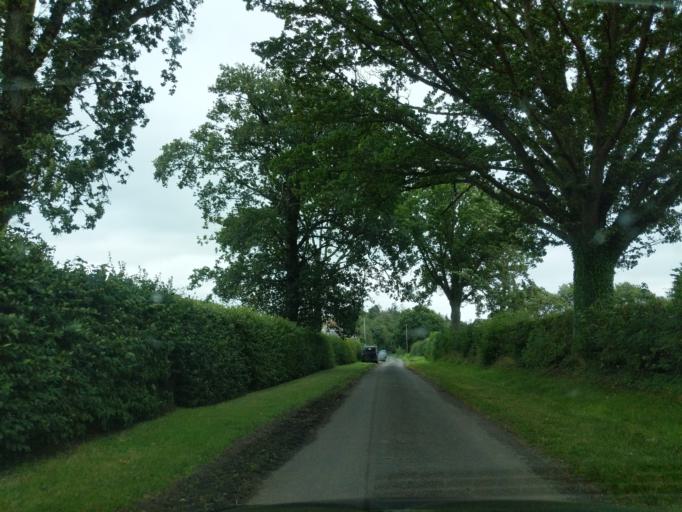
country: GB
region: Scotland
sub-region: The Scottish Borders
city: Kelso
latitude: 55.6198
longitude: -2.4673
